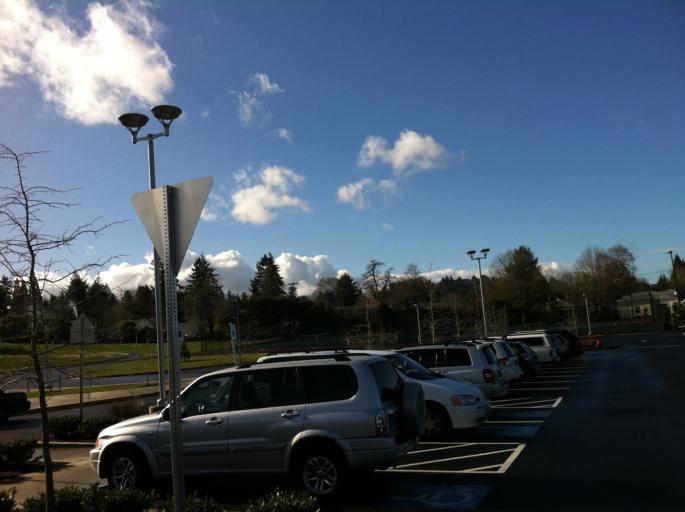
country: US
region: Oregon
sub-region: Multnomah County
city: Lents
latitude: 45.5505
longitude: -122.5408
